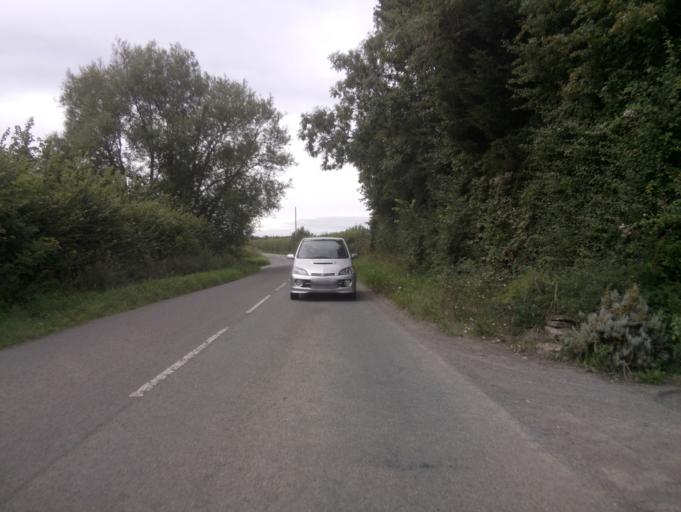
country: GB
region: England
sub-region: Somerset
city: Street
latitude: 51.1150
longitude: -2.7069
